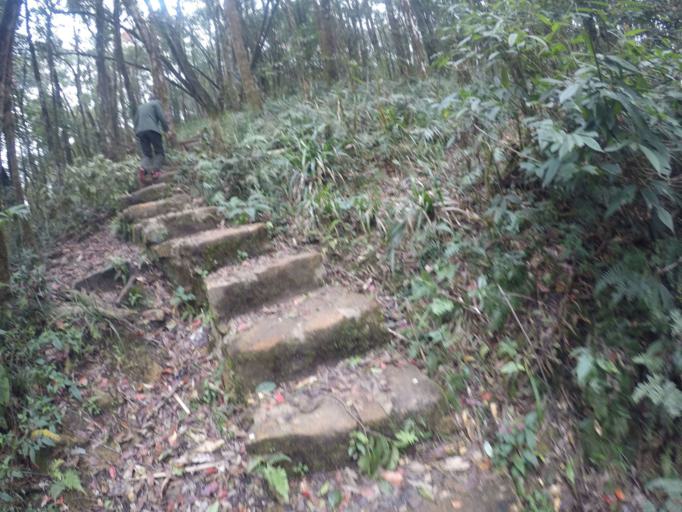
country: VN
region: Lao Cai
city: Sa Pa
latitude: 22.3489
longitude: 103.7744
